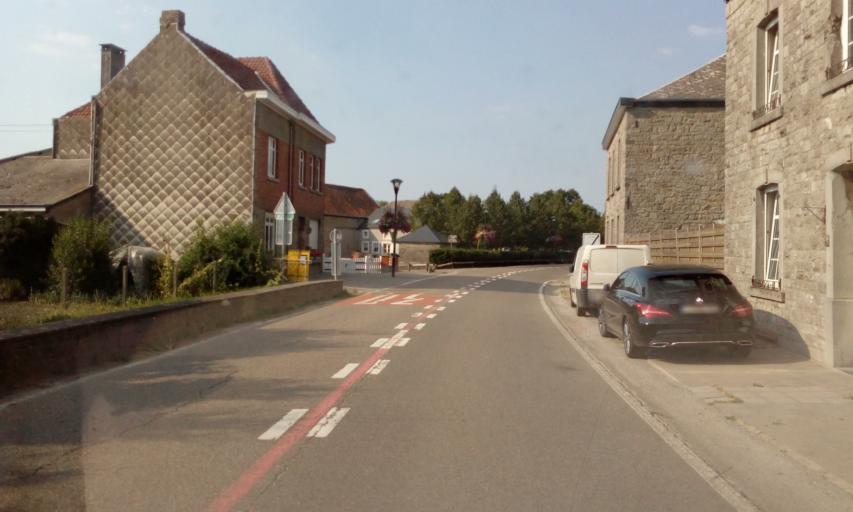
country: BE
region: Wallonia
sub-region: Province de Namur
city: Rochefort
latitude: 50.1201
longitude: 5.2480
